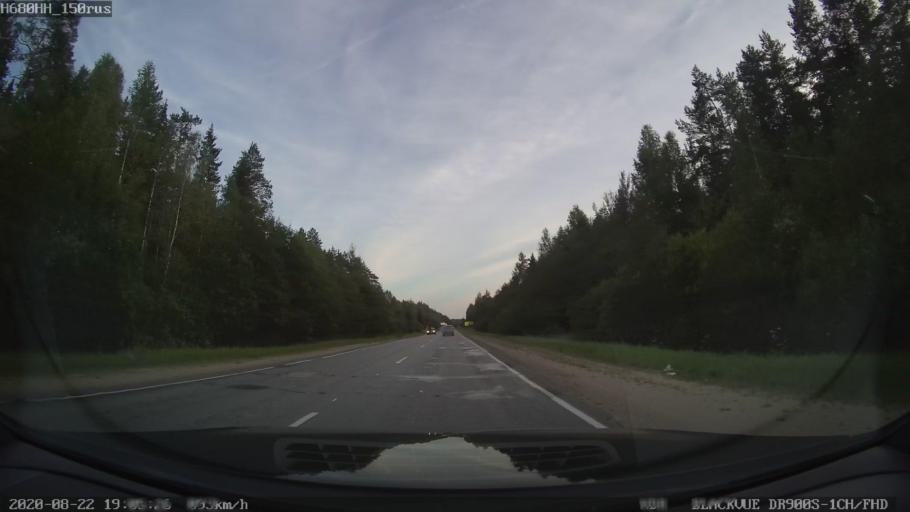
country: RU
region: Tverskaya
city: Sakharovo
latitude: 57.0765
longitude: 36.1118
